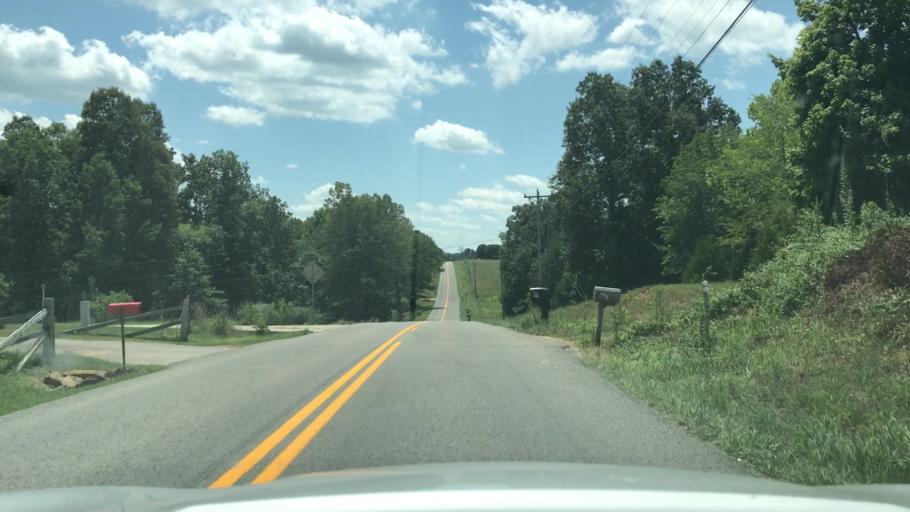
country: US
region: Kentucky
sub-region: Christian County
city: Hopkinsville
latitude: 36.9817
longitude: -87.3605
